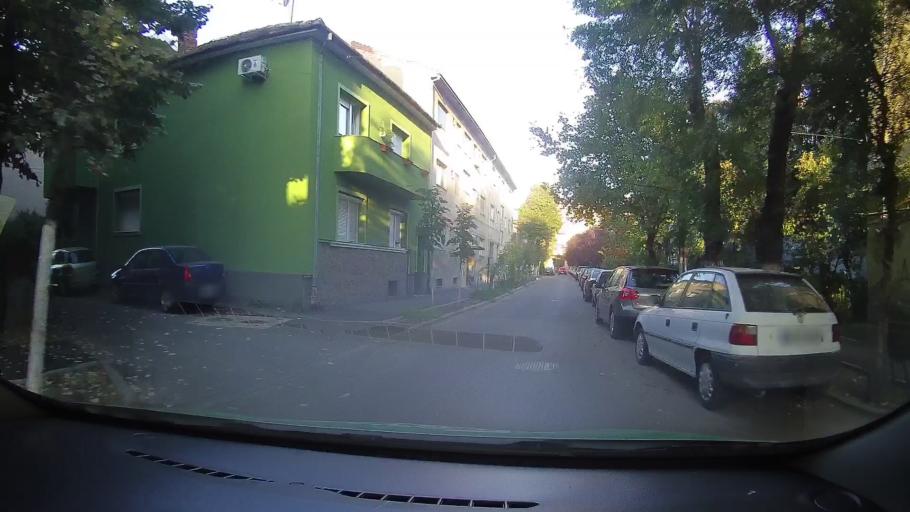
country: RO
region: Arad
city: Arad
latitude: 46.1810
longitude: 21.3247
